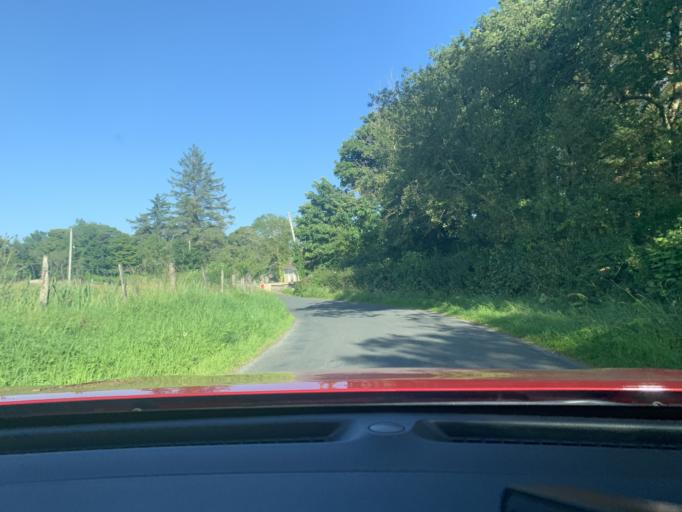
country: IE
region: Connaught
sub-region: Sligo
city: Tobercurry
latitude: 54.0878
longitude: -8.8056
